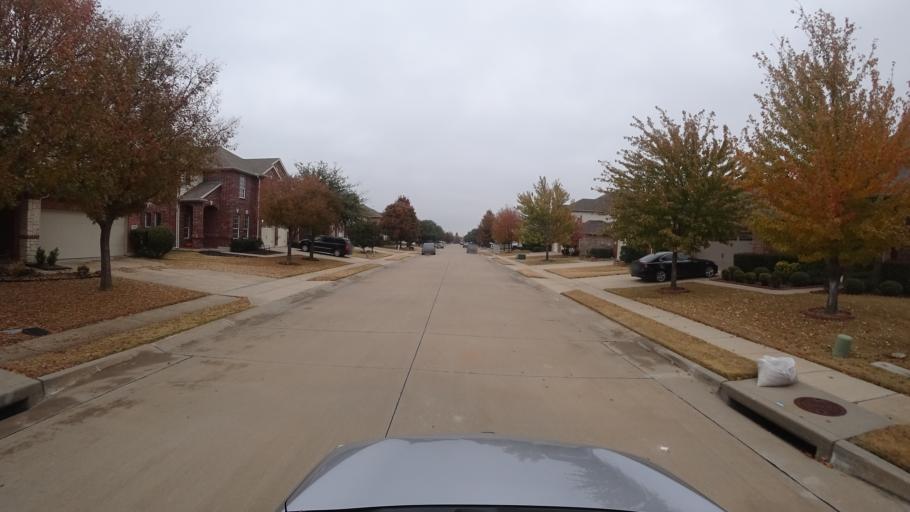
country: US
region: Texas
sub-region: Denton County
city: The Colony
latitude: 33.0677
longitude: -96.9081
